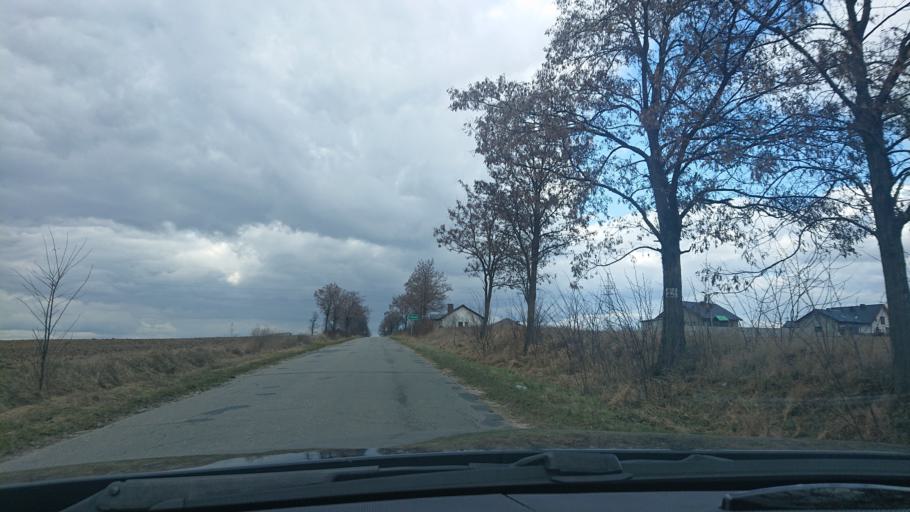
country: PL
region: Greater Poland Voivodeship
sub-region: Powiat gnieznienski
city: Niechanowo
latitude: 52.5597
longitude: 17.6979
